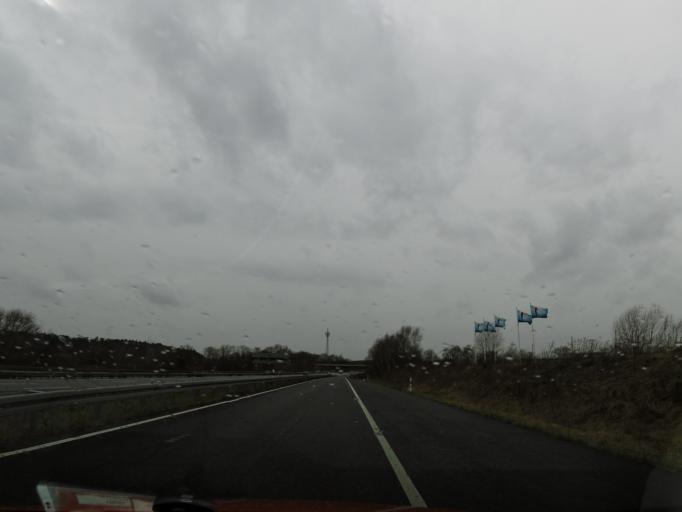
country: DE
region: Brandenburg
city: Rangsdorf
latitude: 52.3072
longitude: 13.4462
